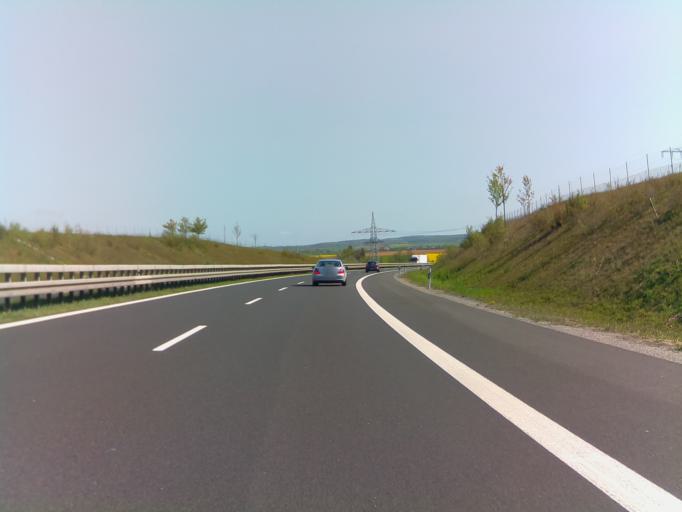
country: DE
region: Bavaria
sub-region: Regierungsbezirk Unterfranken
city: Geldersheim
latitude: 50.0417
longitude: 10.1382
